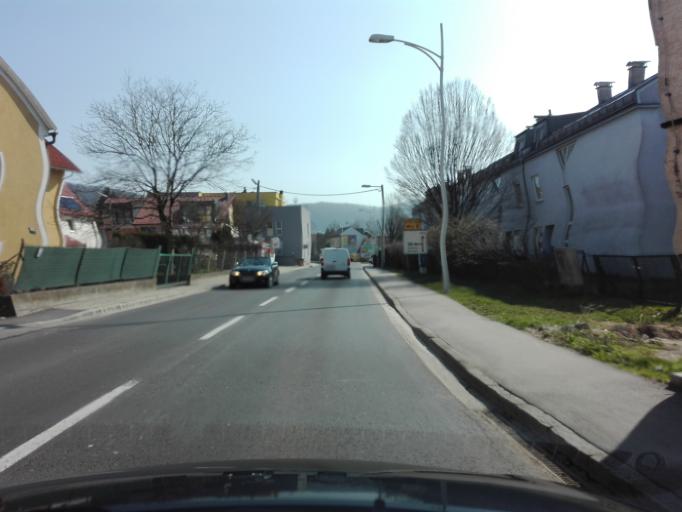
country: AT
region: Upper Austria
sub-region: Linz Stadt
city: Linz
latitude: 48.3278
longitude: 14.3297
